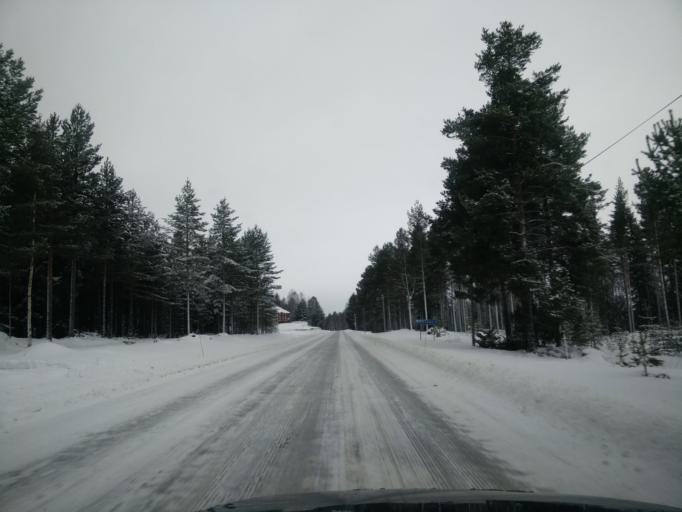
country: SE
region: Vaesternorrland
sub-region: Ange Kommun
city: Ange
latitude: 62.3954
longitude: 15.3785
